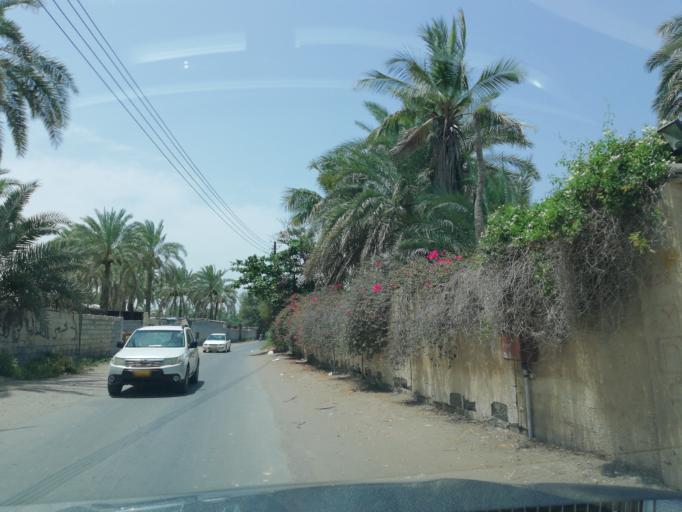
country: OM
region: Muhafazat Masqat
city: As Sib al Jadidah
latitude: 23.6612
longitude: 58.2084
